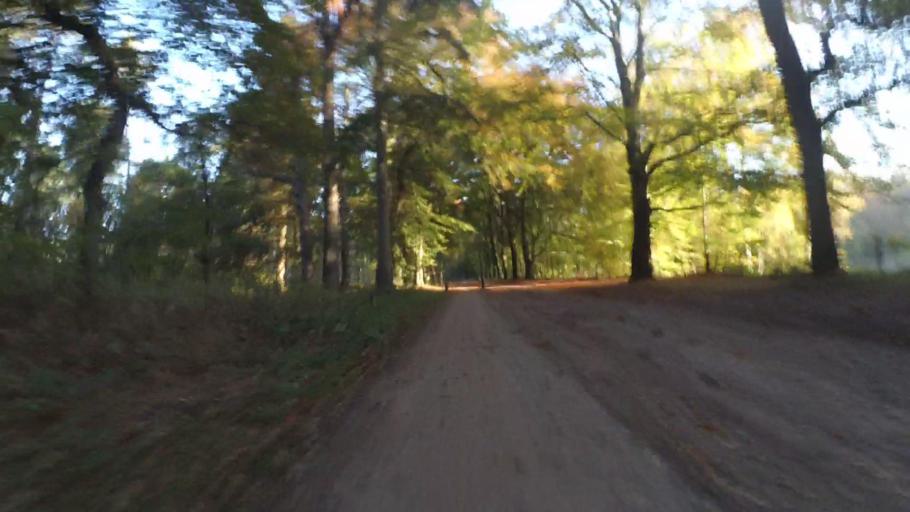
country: NL
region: Utrecht
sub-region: Gemeente Soest
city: Soest
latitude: 52.1861
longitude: 5.2314
